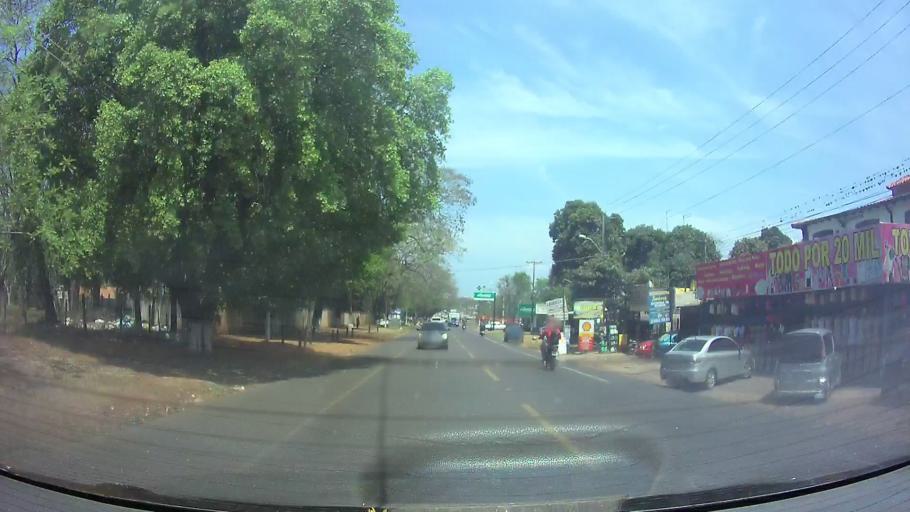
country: PY
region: Central
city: Capiata
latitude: -25.4135
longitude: -57.4581
